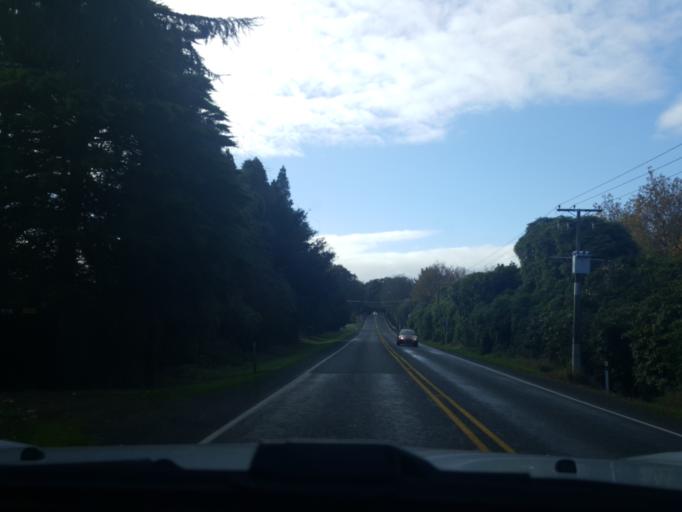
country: NZ
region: Waikato
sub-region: Waipa District
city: Cambridge
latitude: -37.6449
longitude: 175.5528
